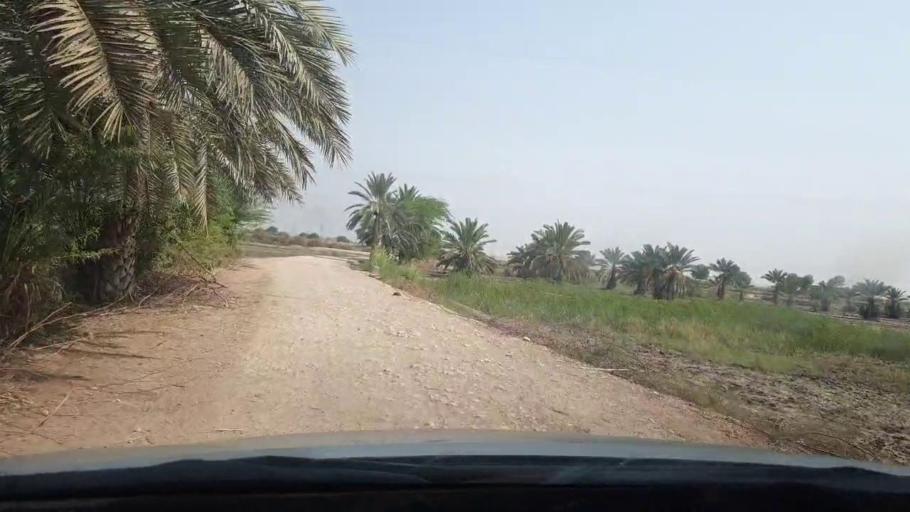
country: PK
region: Sindh
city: Rohri
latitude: 27.6330
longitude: 68.8852
